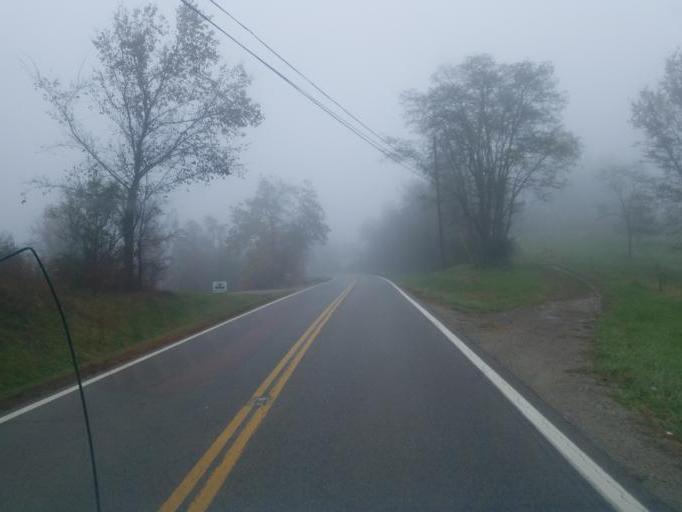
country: US
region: Ohio
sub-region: Morgan County
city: McConnelsville
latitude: 39.6297
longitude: -81.8779
